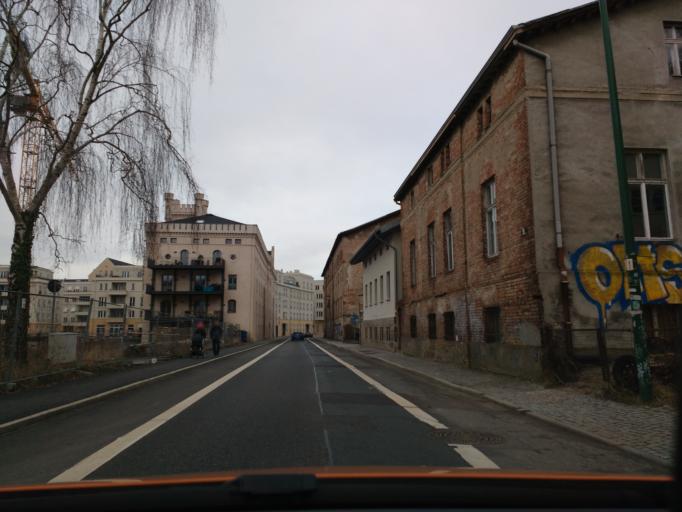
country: DE
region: Brandenburg
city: Potsdam
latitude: 52.3879
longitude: 13.0594
